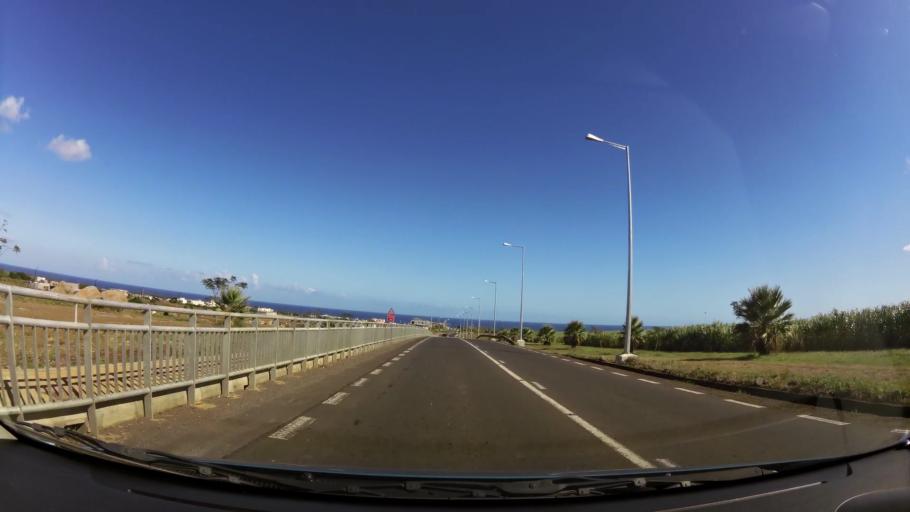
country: MU
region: Black River
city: Cascavelle
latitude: -20.2781
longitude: 57.3891
